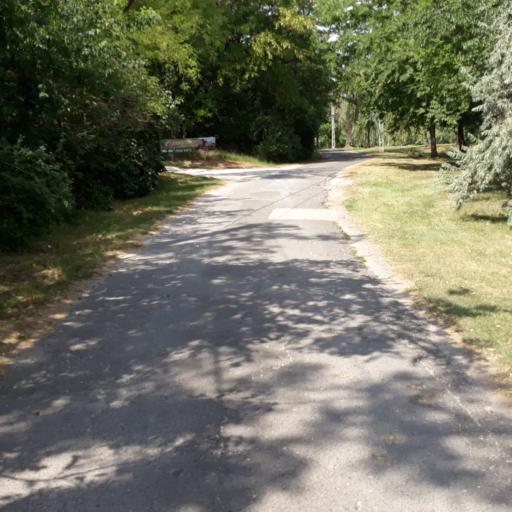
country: HU
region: Bekes
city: Oroshaza
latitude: 46.5620
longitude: 20.6245
